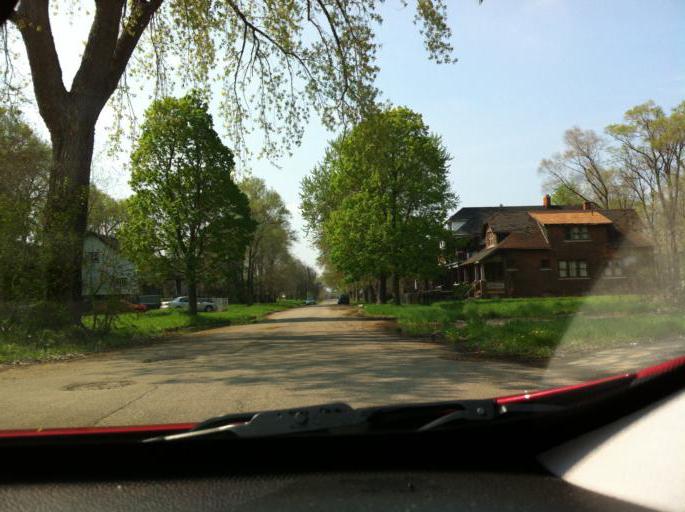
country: US
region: Michigan
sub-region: Wayne County
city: River Rouge
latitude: 42.2990
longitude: -83.1002
